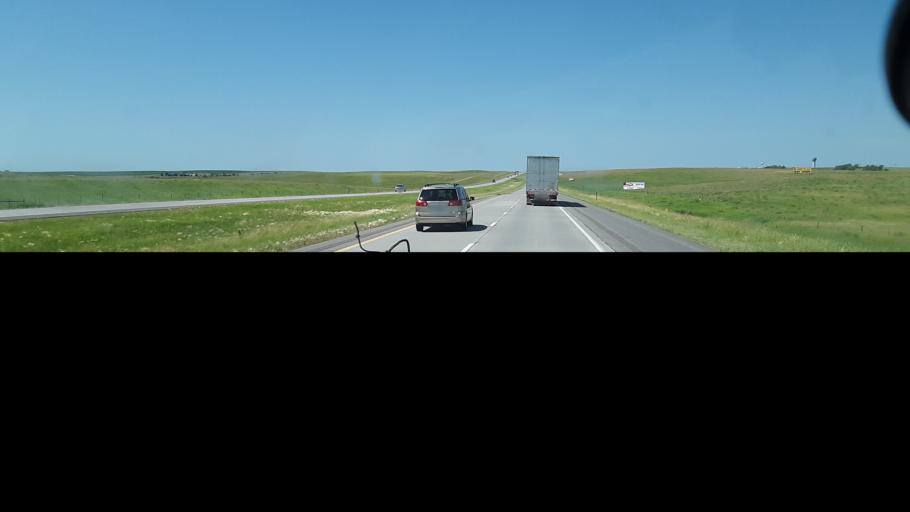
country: US
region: South Dakota
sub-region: Jones County
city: Murdo
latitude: 43.9061
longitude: -100.6458
